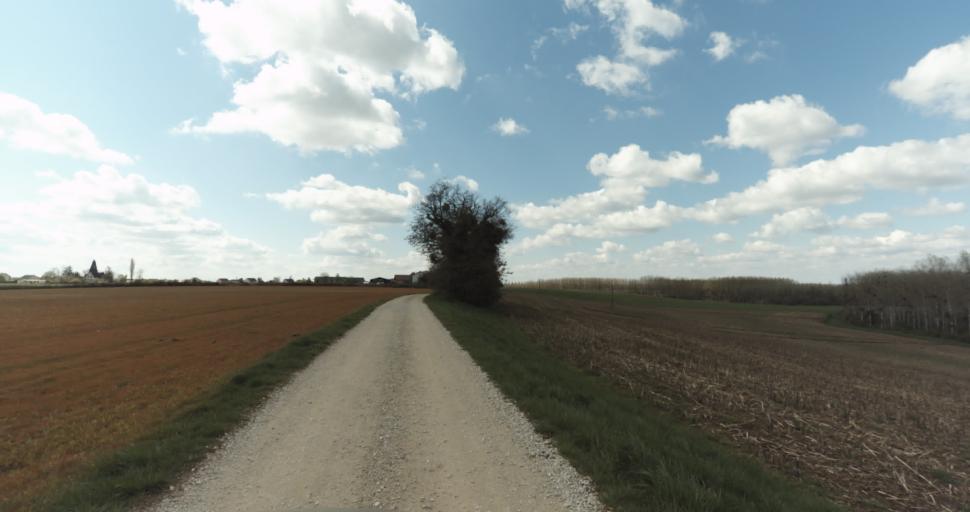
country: FR
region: Bourgogne
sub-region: Departement de la Cote-d'Or
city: Auxonne
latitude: 47.2190
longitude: 5.4214
